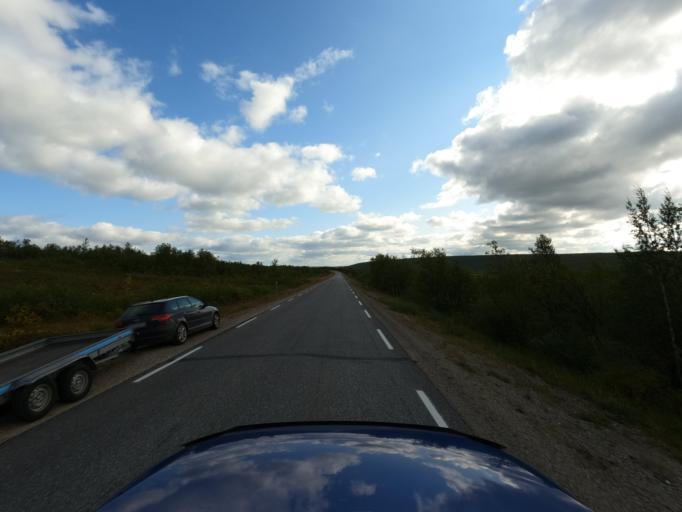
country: NO
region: Finnmark Fylke
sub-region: Porsanger
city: Lakselv
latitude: 69.3739
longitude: 24.4063
